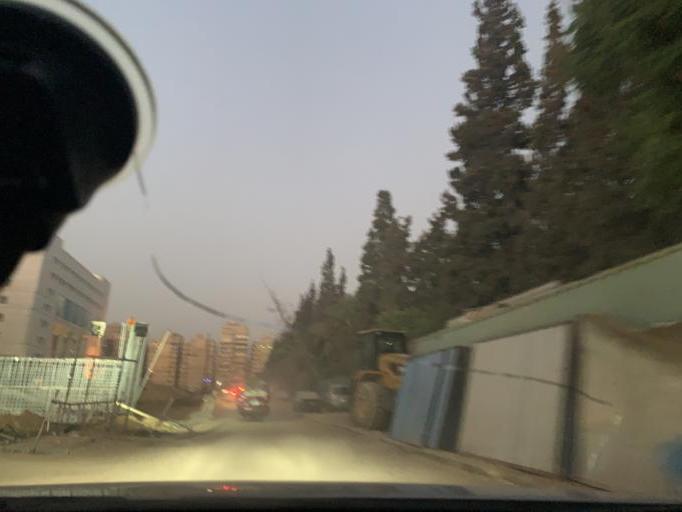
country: EG
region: Muhafazat al Qahirah
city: Cairo
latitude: 30.0630
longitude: 31.3458
